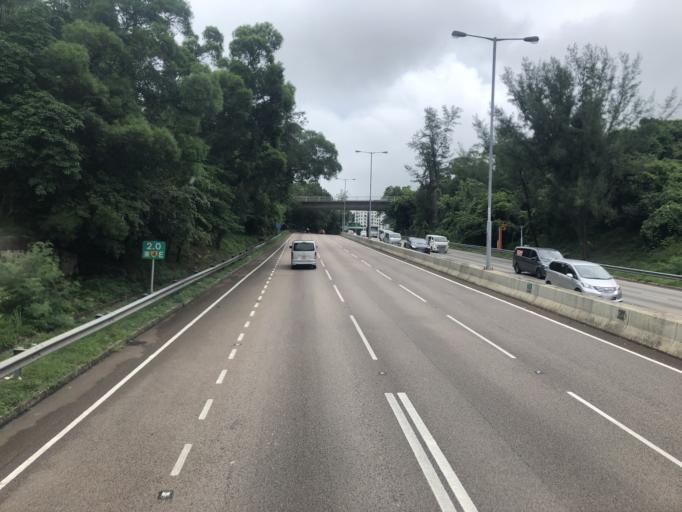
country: HK
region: Wanchai
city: Wan Chai
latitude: 22.2809
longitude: 114.2354
